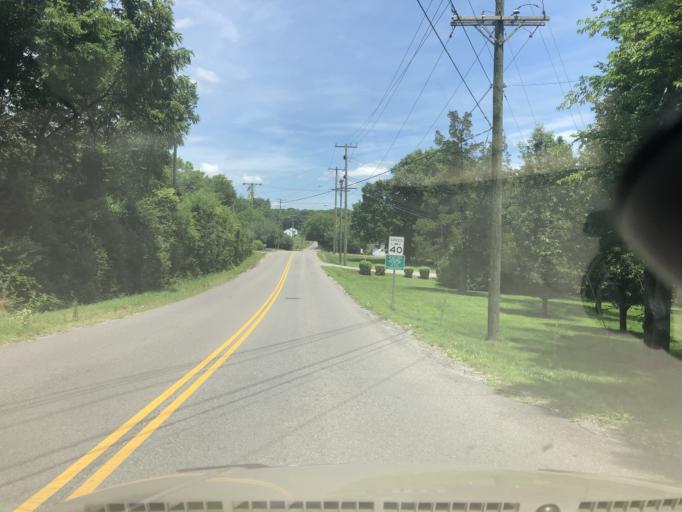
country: US
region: Tennessee
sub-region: Davidson County
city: Lakewood
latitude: 36.2525
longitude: -86.6938
